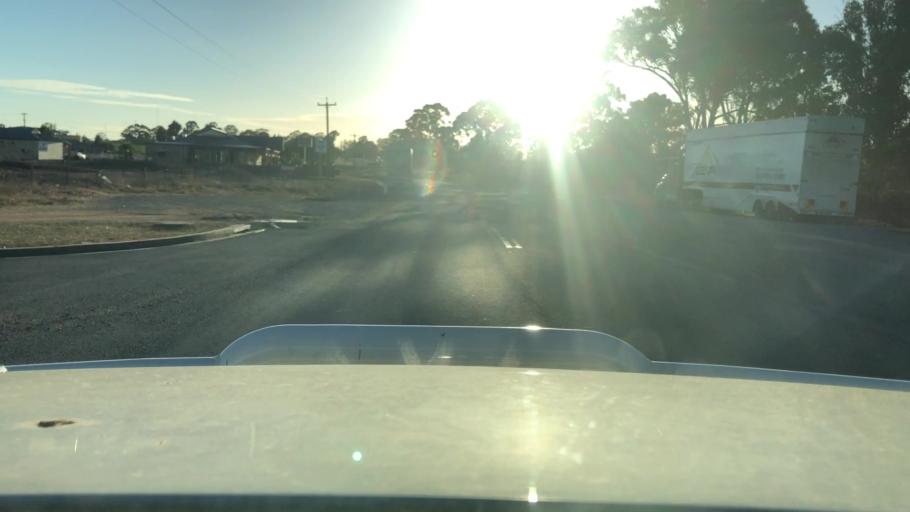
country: AU
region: New South Wales
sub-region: Goulburn Mulwaree
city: Goulburn
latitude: -34.7184
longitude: 149.9977
